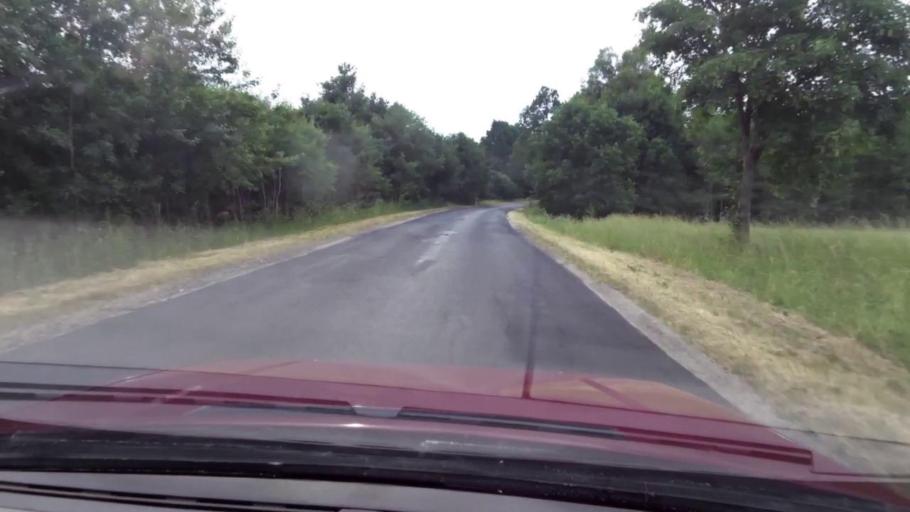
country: PL
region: Pomeranian Voivodeship
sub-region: Powiat slupski
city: Kepice
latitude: 54.2713
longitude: 16.9883
